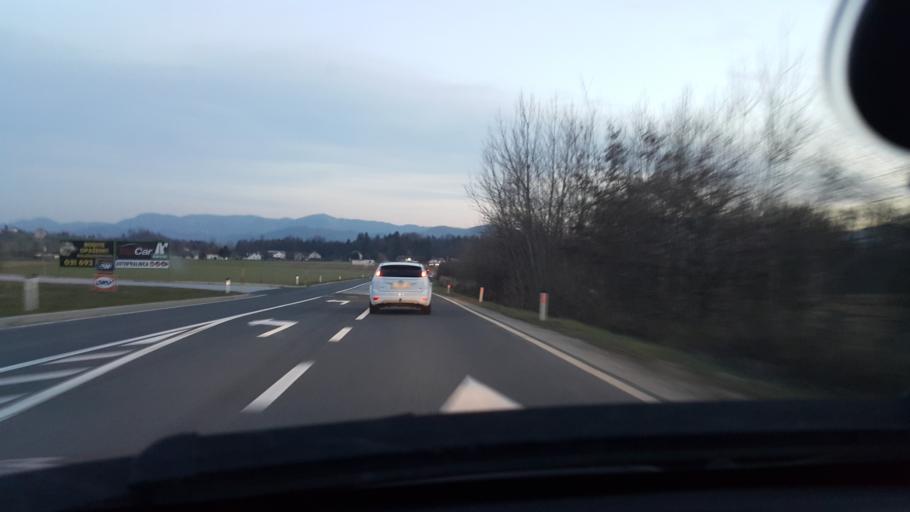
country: SI
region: Zalec
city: Zalec
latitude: 46.2767
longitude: 15.1864
